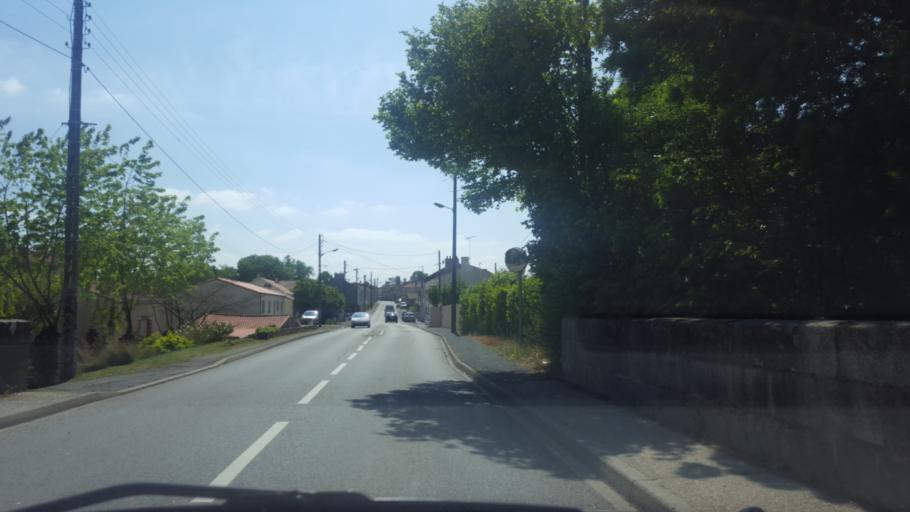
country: FR
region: Pays de la Loire
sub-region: Departement de la Loire-Atlantique
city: La Limouziniere
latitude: 47.0170
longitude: -1.5675
